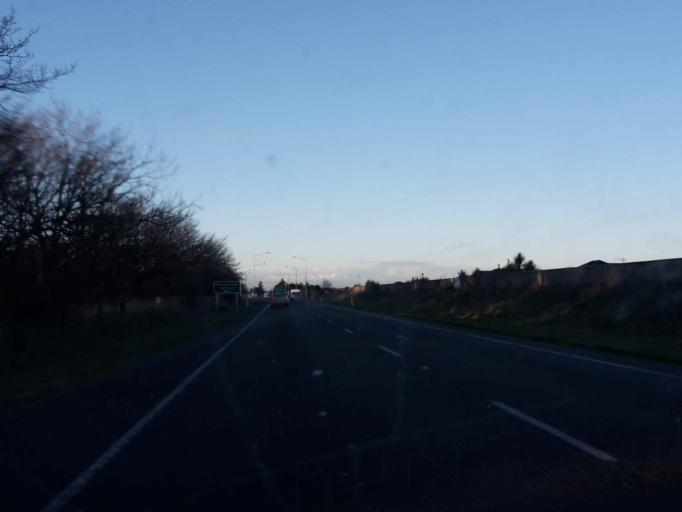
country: NZ
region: Canterbury
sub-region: Selwyn District
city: Rolleston
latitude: -43.5976
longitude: 172.3611
